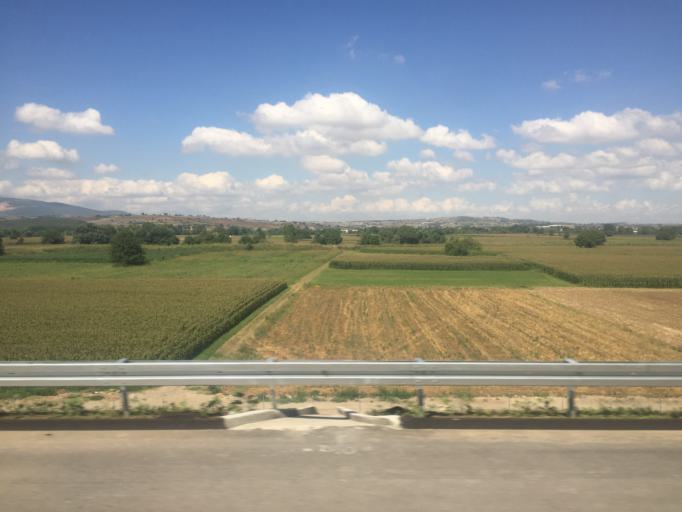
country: TR
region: Balikesir
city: Gobel
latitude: 40.0041
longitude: 28.1944
